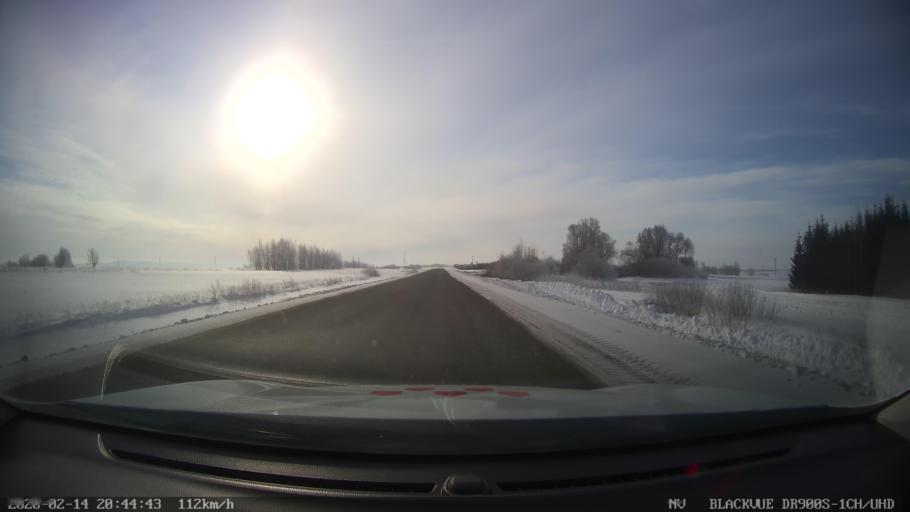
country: RU
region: Tatarstan
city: Kuybyshevskiy Zaton
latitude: 55.2890
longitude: 49.1452
